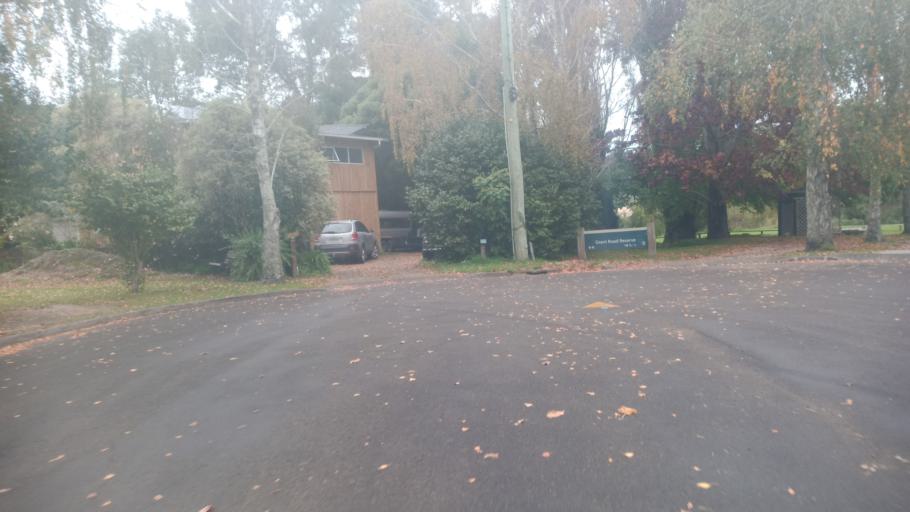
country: NZ
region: Gisborne
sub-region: Gisborne District
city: Gisborne
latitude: -38.6658
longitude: 178.0398
